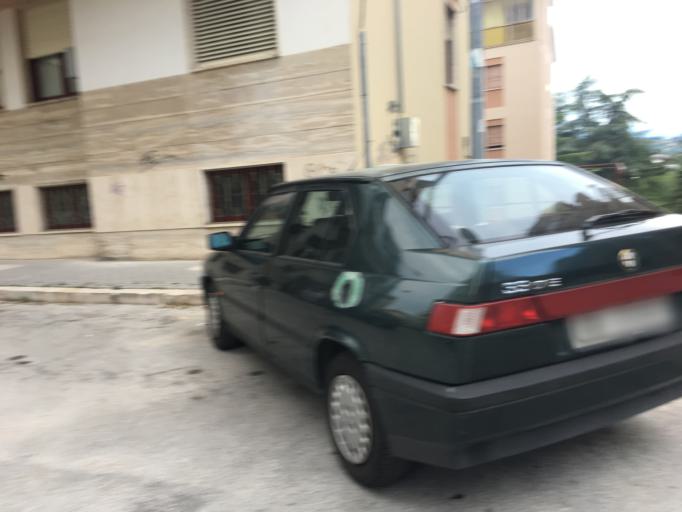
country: IT
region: Molise
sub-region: Provincia di Campobasso
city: Campobasso
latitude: 41.5569
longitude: 14.6555
